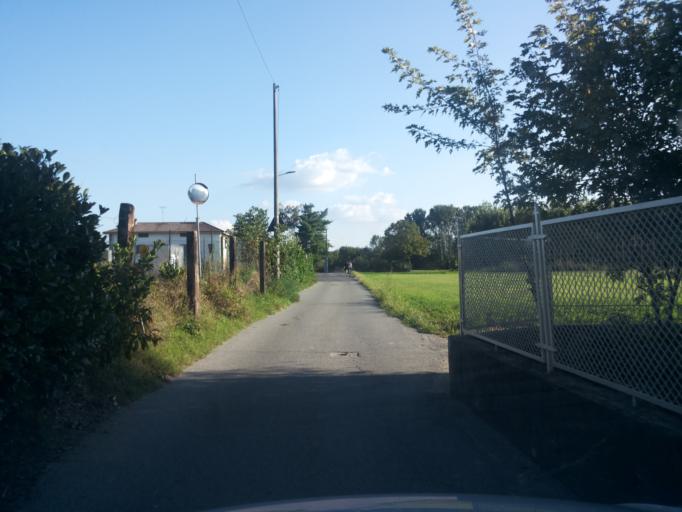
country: IT
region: Piedmont
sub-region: Provincia di Torino
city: Strambino
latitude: 45.3963
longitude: 7.8965
